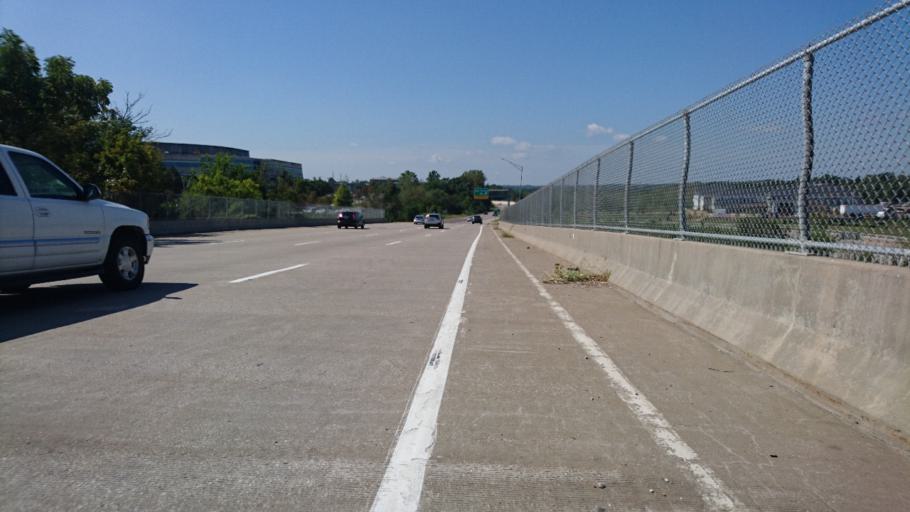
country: US
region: Missouri
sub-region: Saint Louis County
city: Town and Country
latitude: 38.6040
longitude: -90.4541
